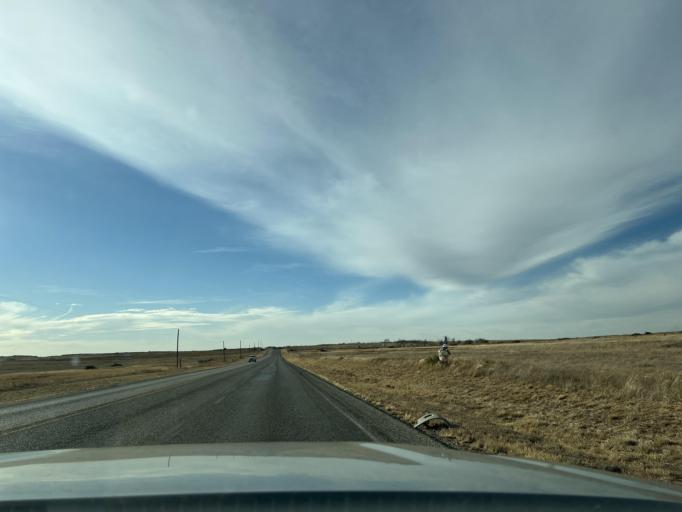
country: US
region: Texas
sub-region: Fisher County
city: Rotan
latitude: 32.7395
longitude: -100.5292
